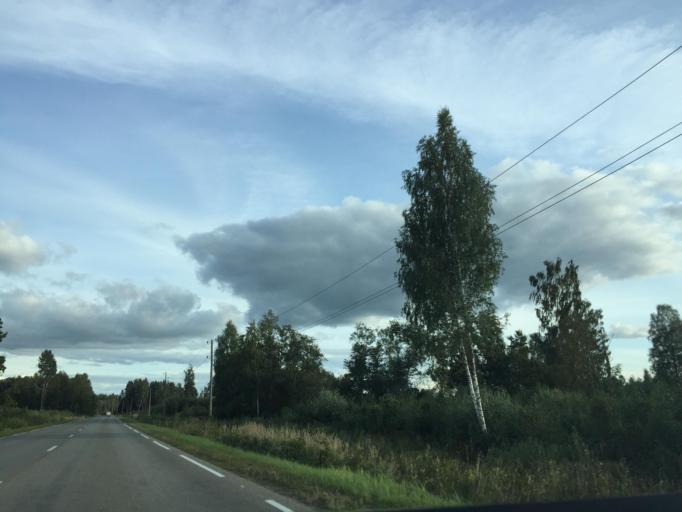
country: LV
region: Nereta
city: Nereta
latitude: 56.3013
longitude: 25.1072
